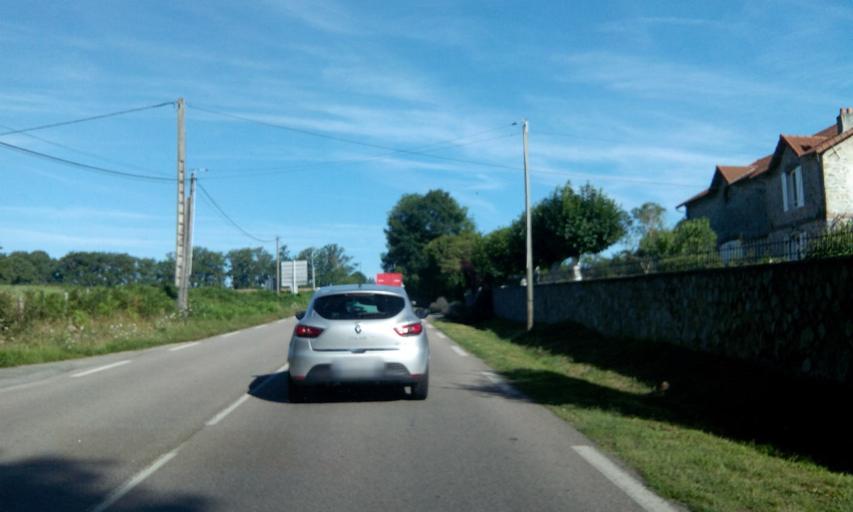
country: FR
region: Limousin
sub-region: Departement de la Haute-Vienne
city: Saint-Leonard-de-Noblat
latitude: 45.8411
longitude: 1.4654
